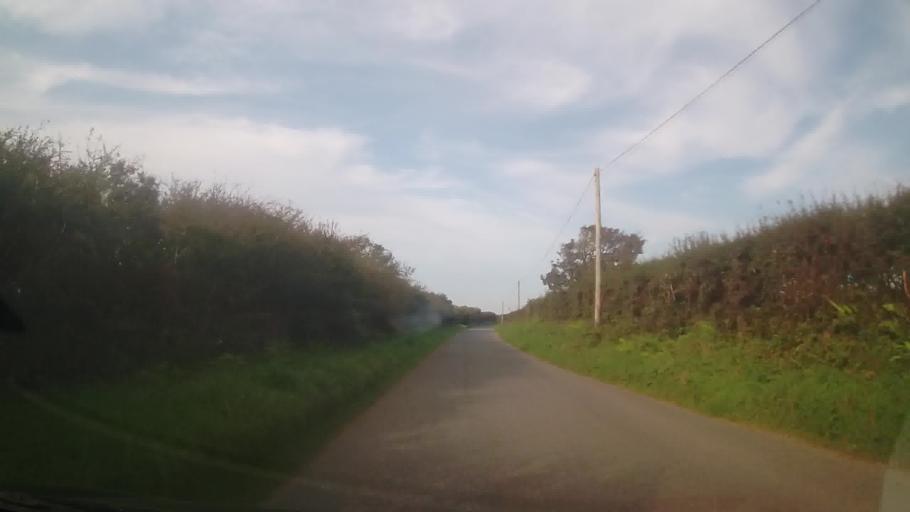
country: GB
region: Wales
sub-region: Pembrokeshire
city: Camrose
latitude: 51.8714
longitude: -5.0497
